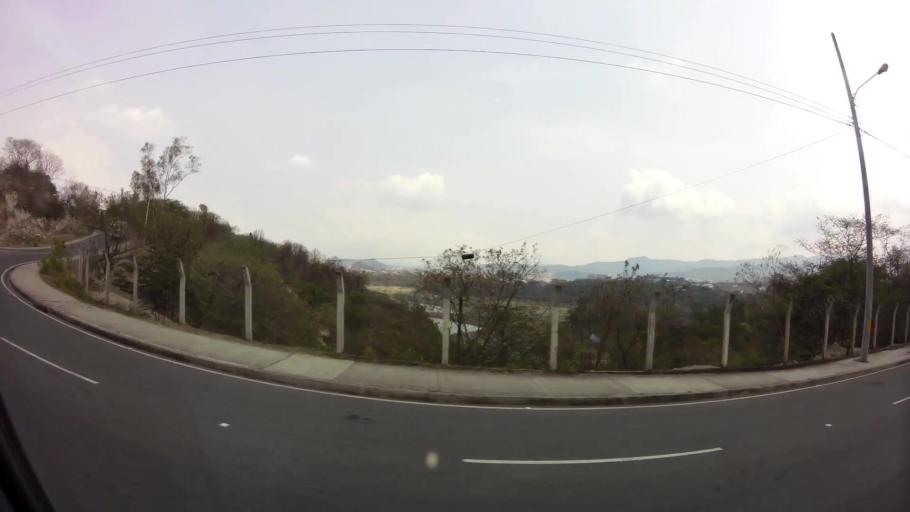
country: HN
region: Francisco Morazan
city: Tegucigalpa
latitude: 14.0706
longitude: -87.2467
